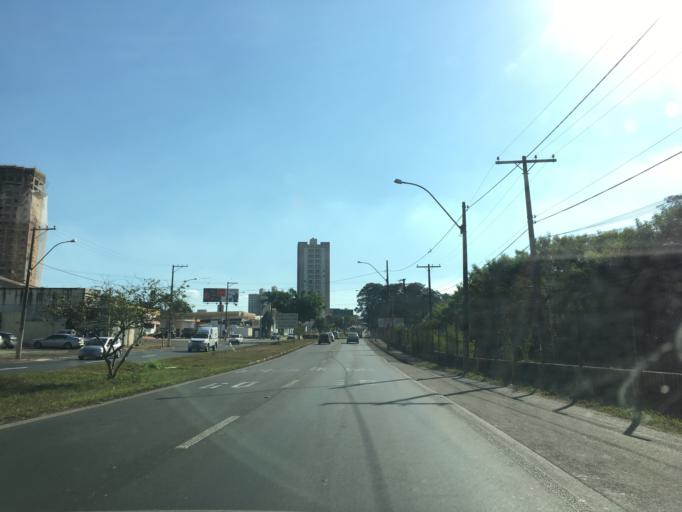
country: BR
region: Sao Paulo
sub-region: Piracicaba
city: Piracicaba
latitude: -22.7162
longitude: -47.6267
